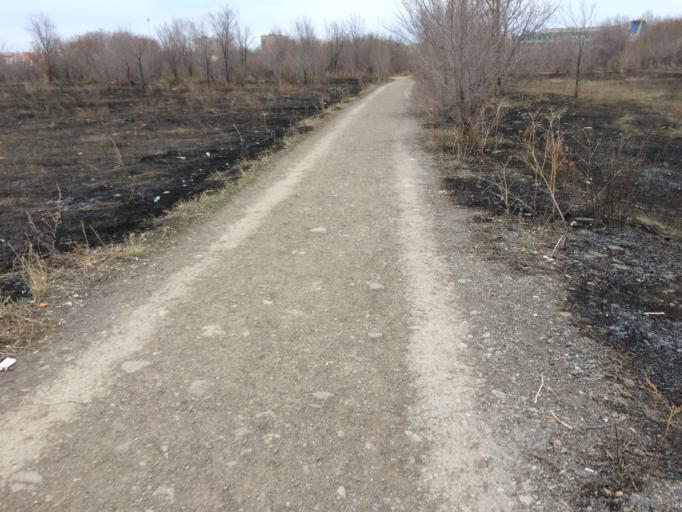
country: RU
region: Chelyabinsk
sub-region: Gorod Magnitogorsk
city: Magnitogorsk
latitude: 53.4417
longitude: 58.9765
